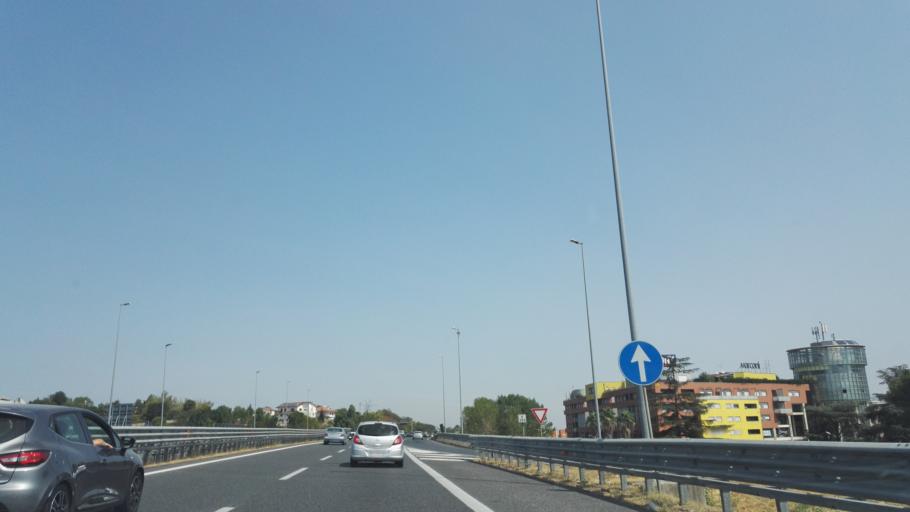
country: IT
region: Calabria
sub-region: Provincia di Cosenza
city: Quattromiglia
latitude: 39.3516
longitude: 16.2341
